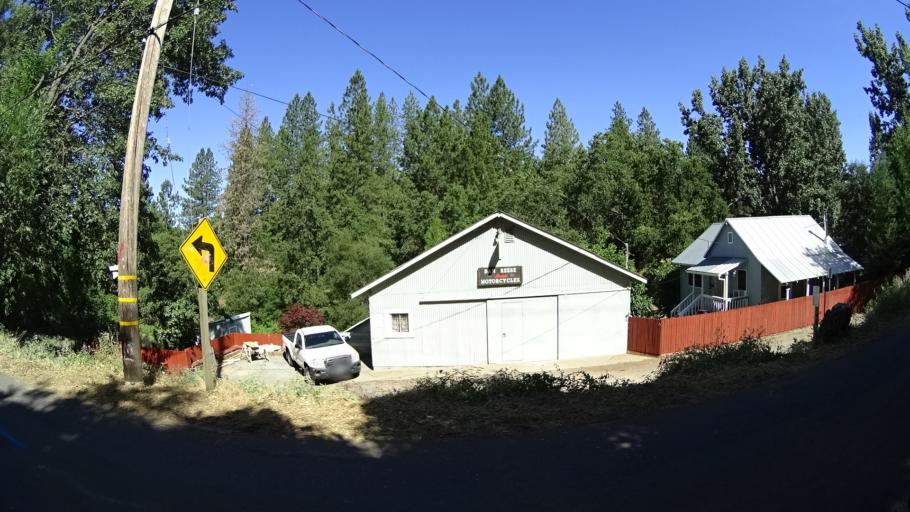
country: US
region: California
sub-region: Amador County
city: Pioneer
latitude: 38.3994
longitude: -120.5303
